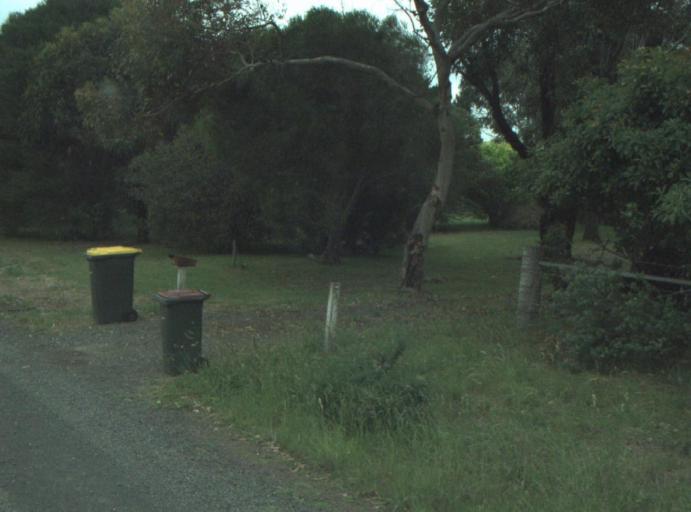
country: AU
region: Victoria
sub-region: Greater Geelong
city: Leopold
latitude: -38.1996
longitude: 144.4668
